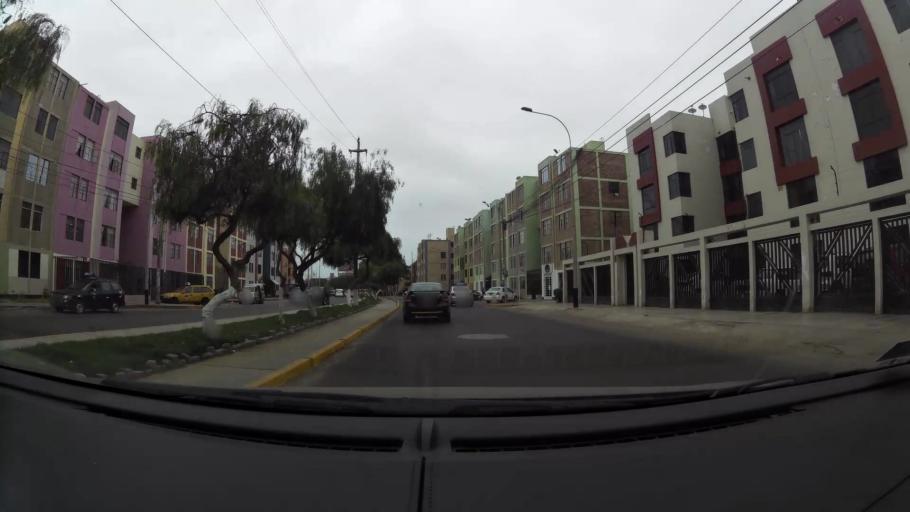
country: PE
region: La Libertad
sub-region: Provincia de Trujillo
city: Trujillo
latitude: -8.1243
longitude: -79.0299
